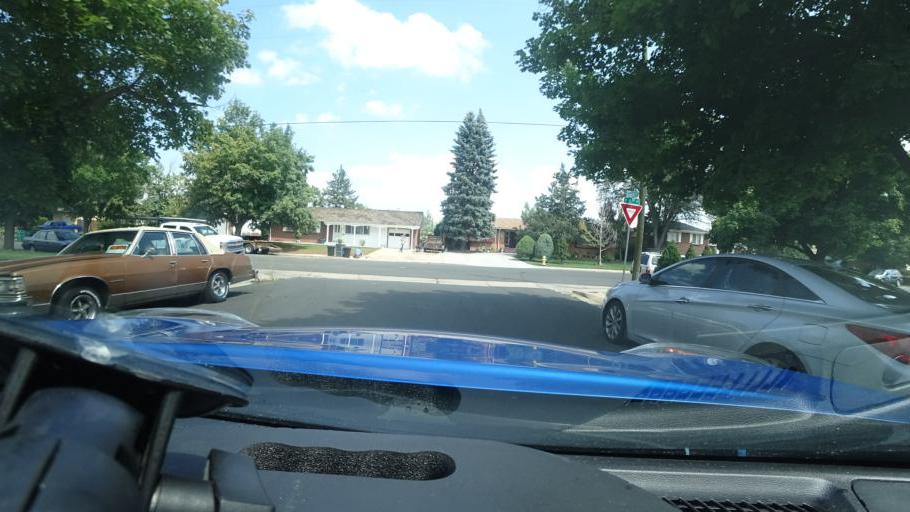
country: US
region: Colorado
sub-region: Adams County
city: Aurora
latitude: 39.7247
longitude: -104.8550
